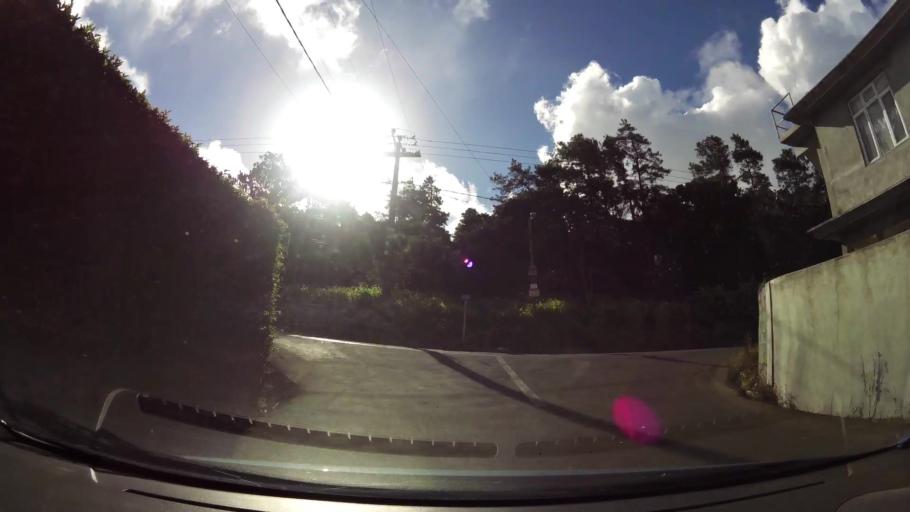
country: MU
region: Plaines Wilhems
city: Curepipe
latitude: -20.3215
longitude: 57.5135
